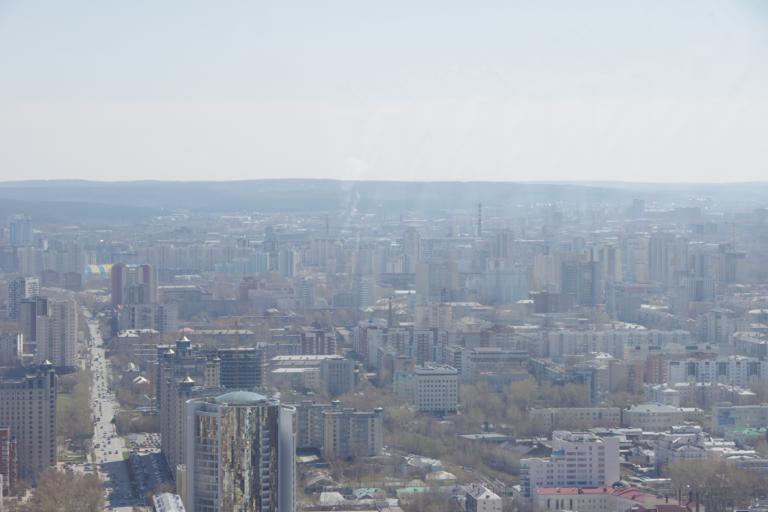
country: RU
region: Sverdlovsk
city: Yekaterinburg
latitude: 56.8360
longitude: 60.6143
